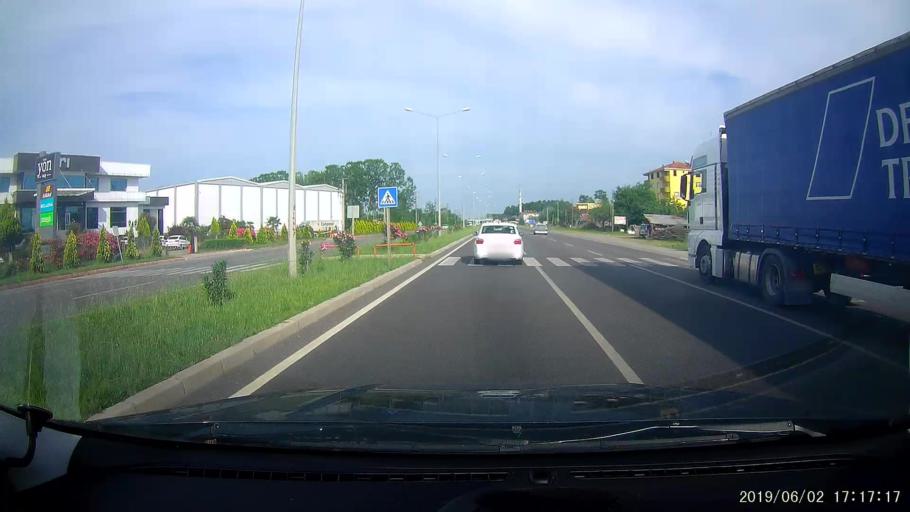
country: TR
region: Samsun
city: Dikbiyik
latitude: 41.2300
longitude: 36.5789
